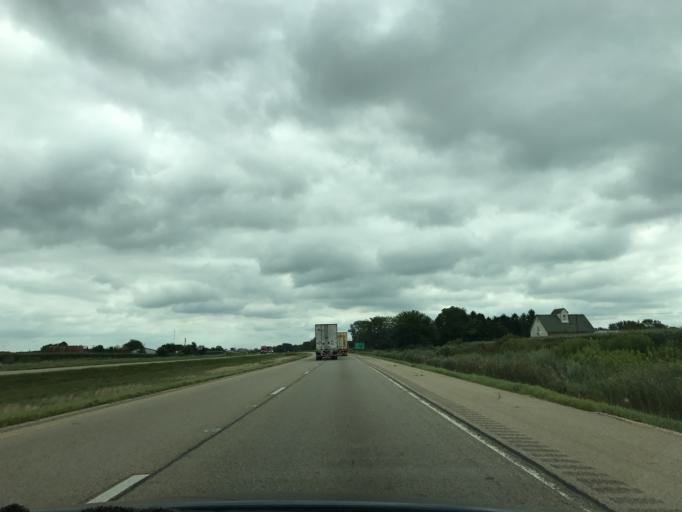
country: US
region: Illinois
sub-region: Bureau County
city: Ladd
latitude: 41.3651
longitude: -89.2046
